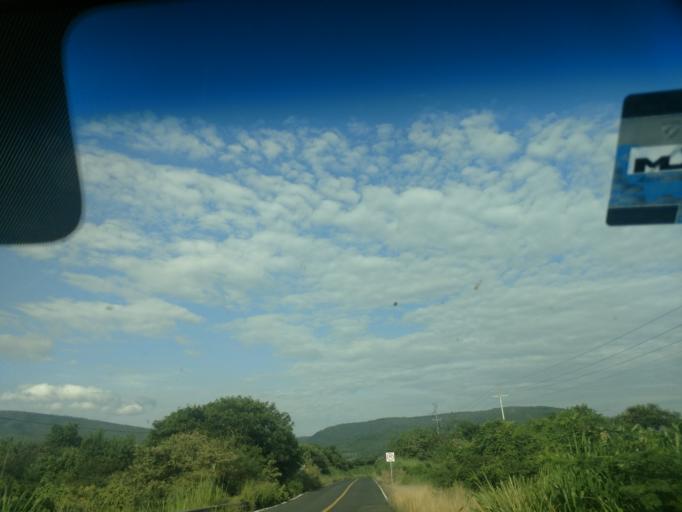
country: MX
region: Jalisco
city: Ameca
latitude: 20.5200
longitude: -104.1164
